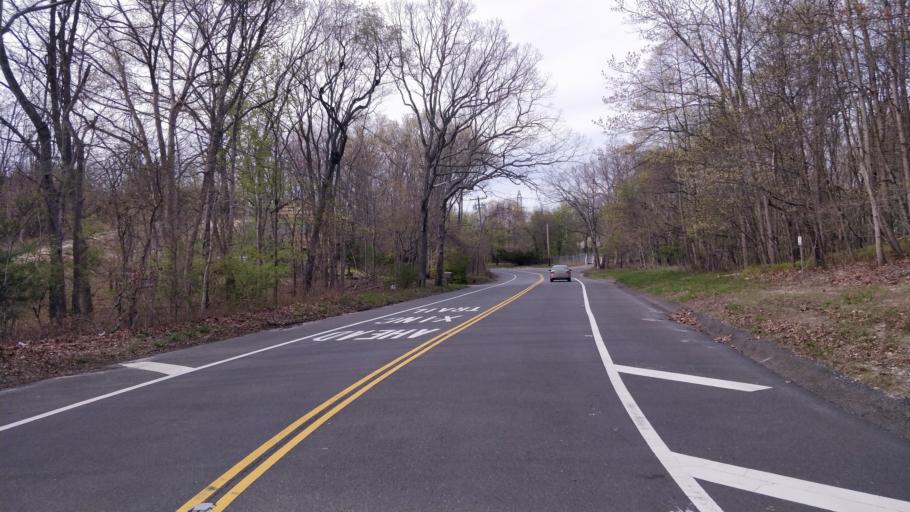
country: US
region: New York
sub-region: Suffolk County
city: Setauket-East Setauket
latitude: 40.9283
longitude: -73.0874
